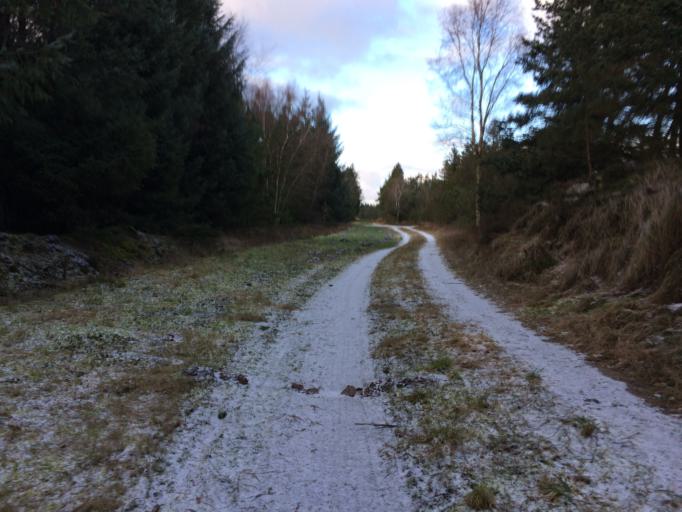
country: DK
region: Central Jutland
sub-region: Holstebro Kommune
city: Ulfborg
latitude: 56.2629
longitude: 8.3957
